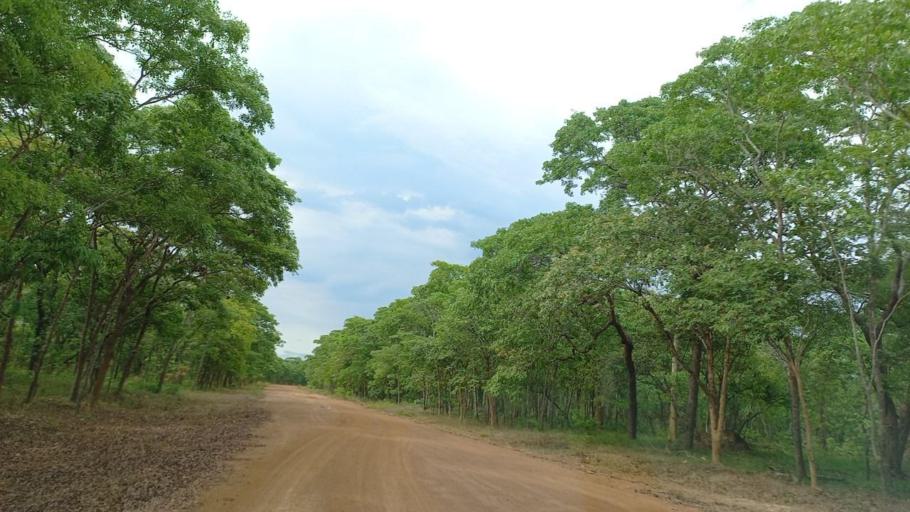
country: ZM
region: North-Western
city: Kalengwa
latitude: -13.3897
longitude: 25.0705
